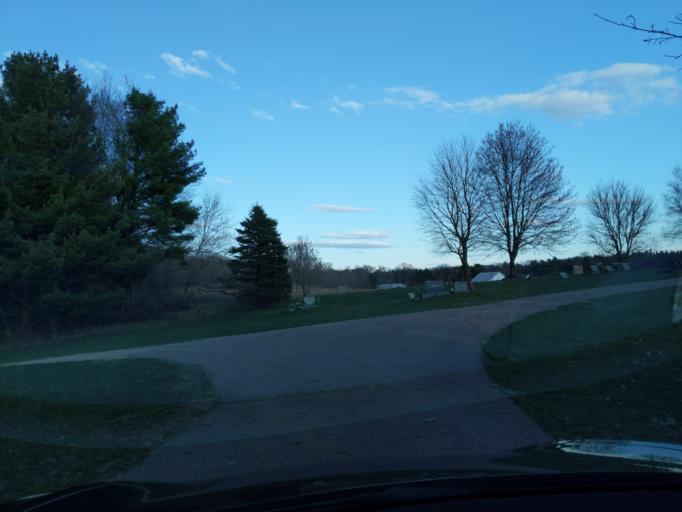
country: US
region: Michigan
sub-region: Ingham County
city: Mason
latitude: 42.5515
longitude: -84.3792
